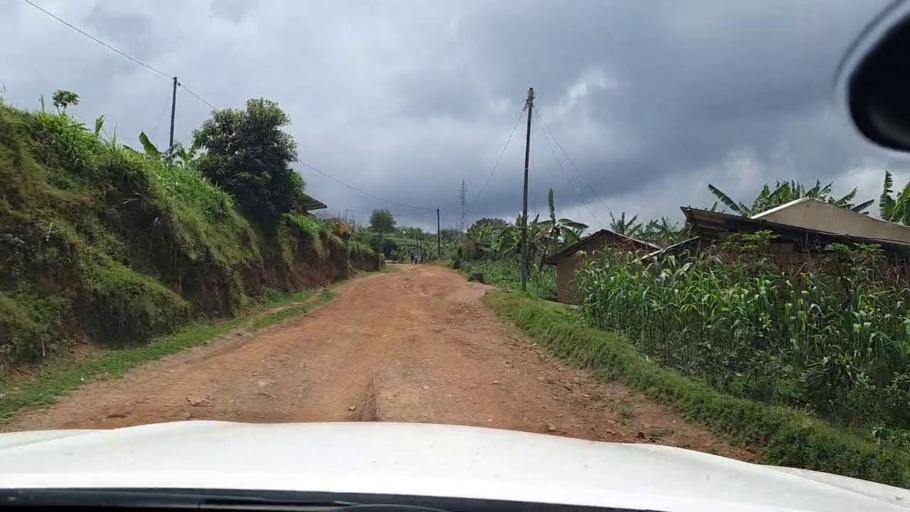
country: RW
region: Western Province
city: Kibuye
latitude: -2.1698
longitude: 29.4317
